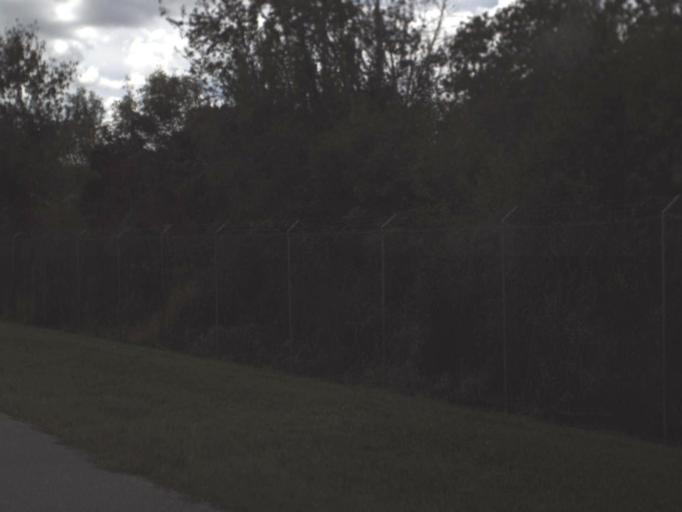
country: US
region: Florida
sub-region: Collier County
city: Orangetree
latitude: 26.0388
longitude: -81.3444
